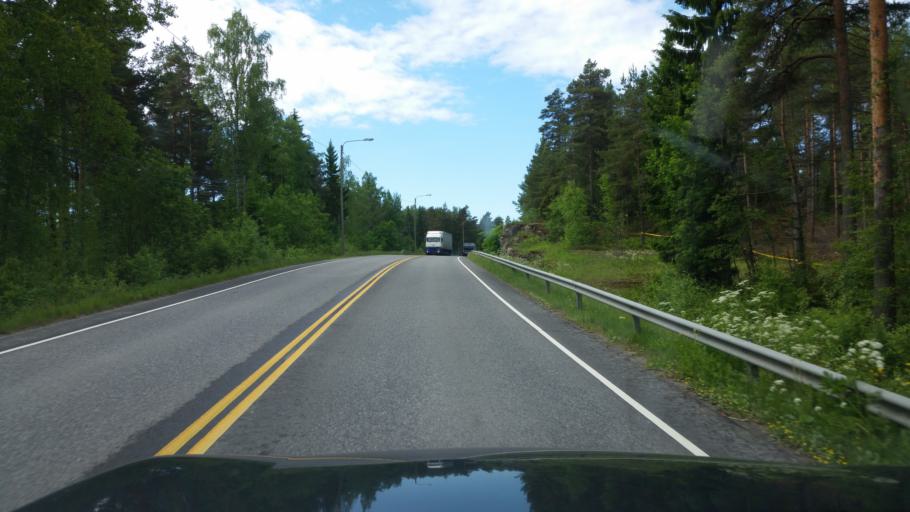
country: FI
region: Varsinais-Suomi
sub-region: Aboland-Turunmaa
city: Pargas
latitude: 60.3335
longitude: 22.3612
